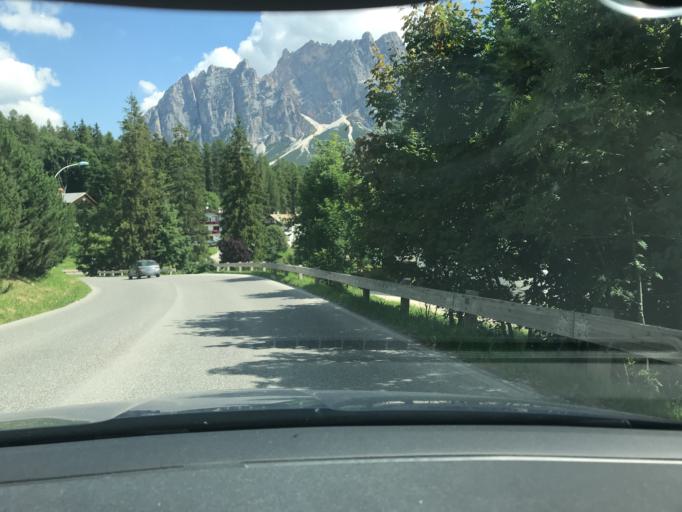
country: IT
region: Veneto
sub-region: Provincia di Belluno
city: Cortina d'Ampezzo
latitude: 46.5414
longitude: 12.1248
